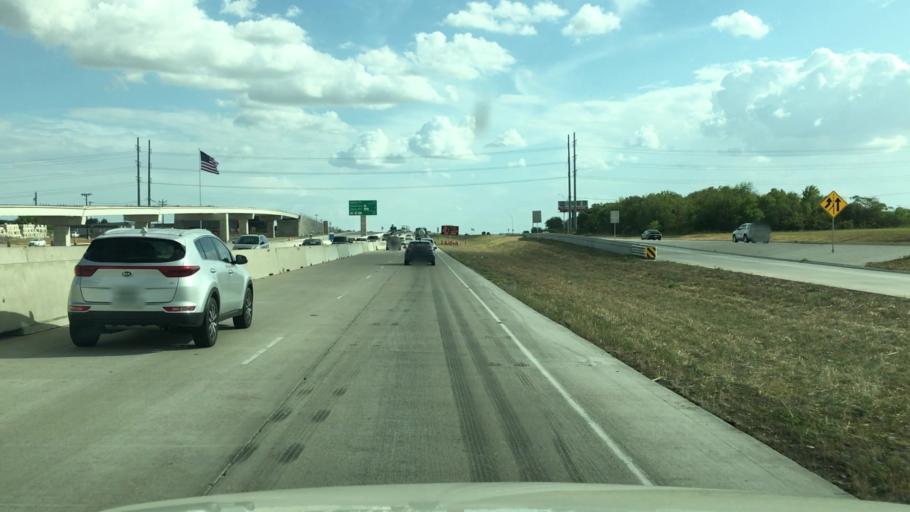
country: US
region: Texas
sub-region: Bell County
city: Temple
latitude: 31.1341
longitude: -97.3320
